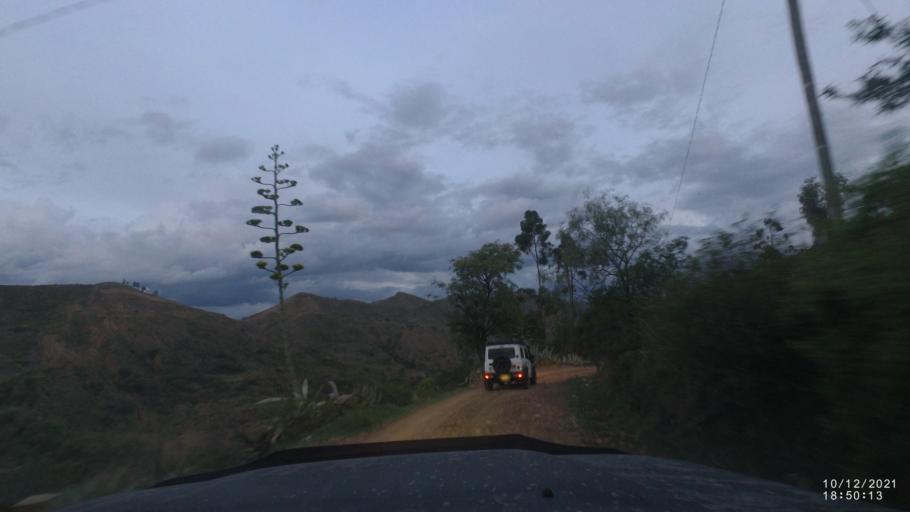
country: BO
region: Cochabamba
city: Tarata
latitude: -17.8813
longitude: -65.9690
